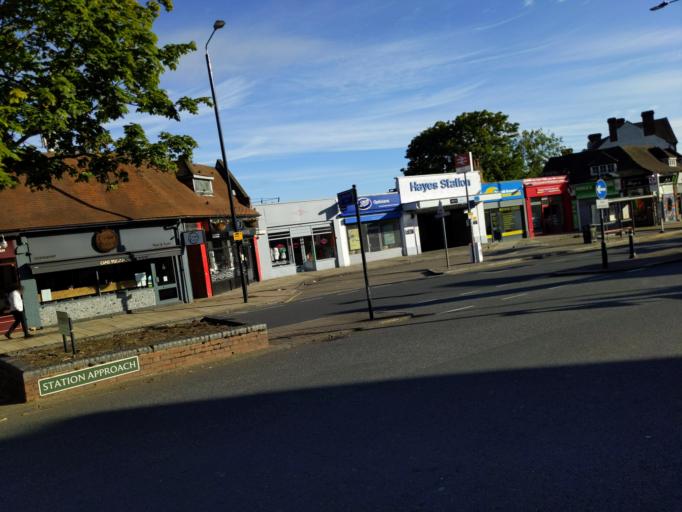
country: GB
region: England
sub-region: Greater London
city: West Wickham
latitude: 51.3759
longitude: 0.0107
